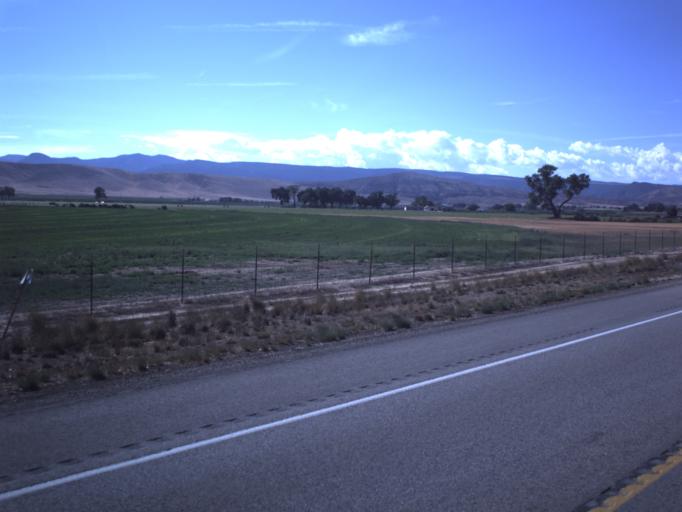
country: US
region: Utah
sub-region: Sanpete County
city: Centerfield
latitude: 39.0796
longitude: -111.8210
